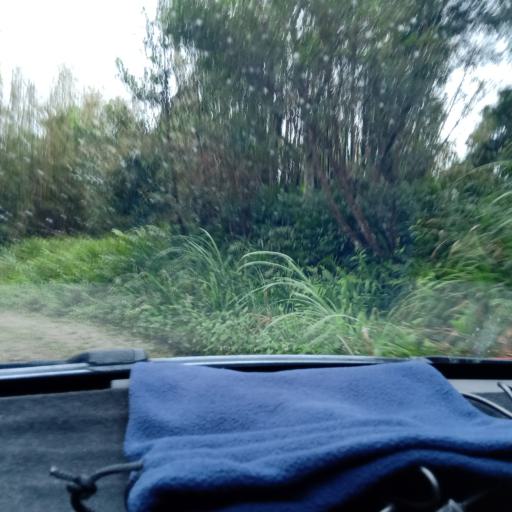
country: TW
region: Taiwan
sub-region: Yilan
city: Yilan
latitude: 24.8130
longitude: 121.6917
